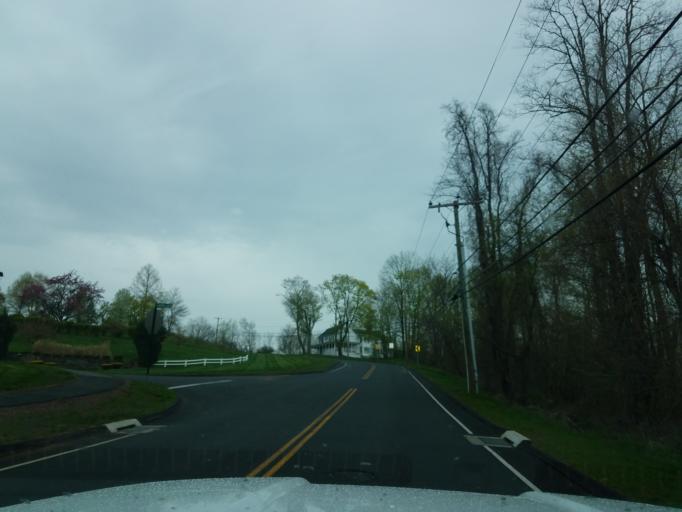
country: US
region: Connecticut
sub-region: Hartford County
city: West Hartford
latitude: 41.7235
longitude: -72.7752
